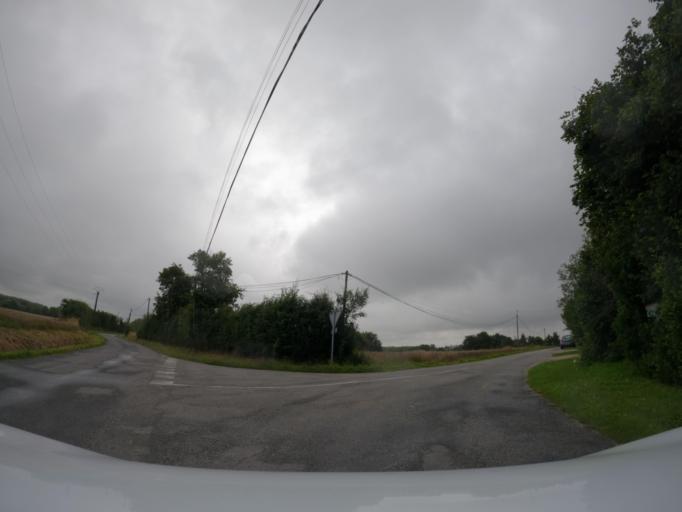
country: FR
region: Pays de la Loire
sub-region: Departement de la Loire-Atlantique
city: Saint-Mars-du-Desert
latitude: 47.3805
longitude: -1.4087
